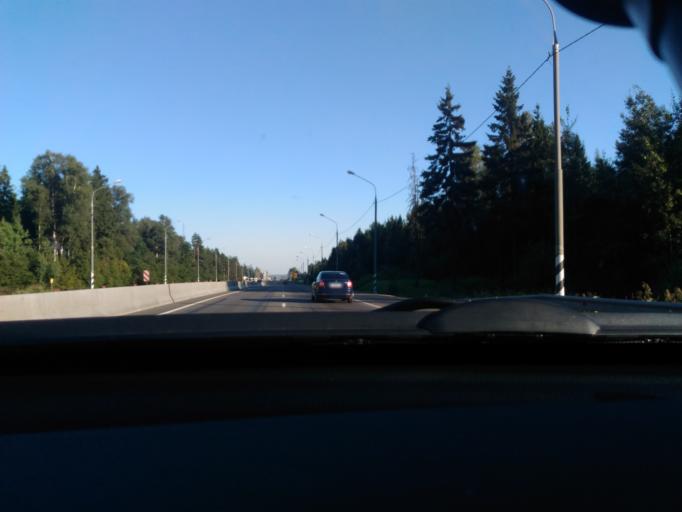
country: RU
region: Moskovskaya
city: Lozhki
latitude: 56.0833
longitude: 37.1196
